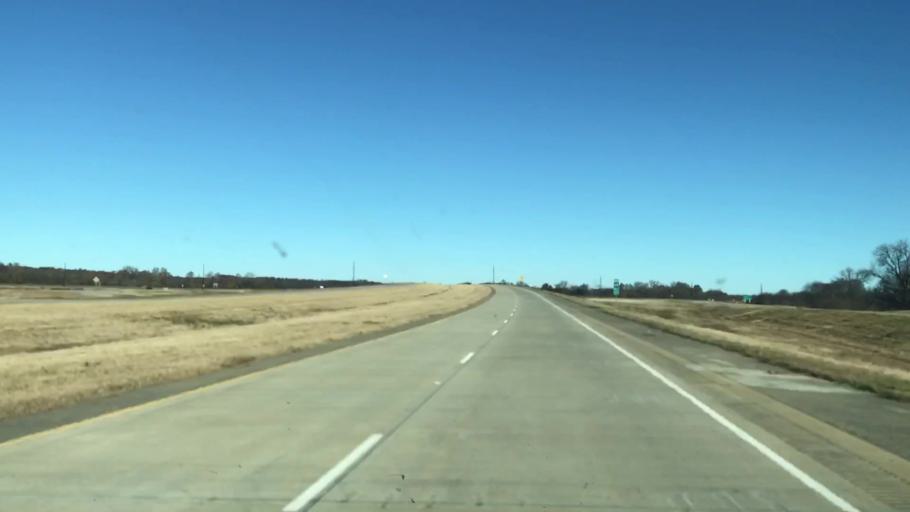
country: US
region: Louisiana
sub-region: Caddo Parish
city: Vivian
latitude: 32.8924
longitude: -93.8603
